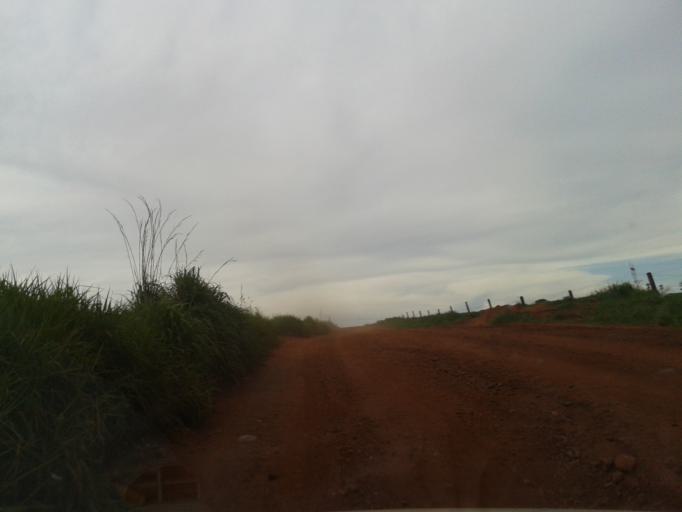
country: BR
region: Minas Gerais
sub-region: Santa Vitoria
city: Santa Vitoria
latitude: -19.0547
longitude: -50.4798
